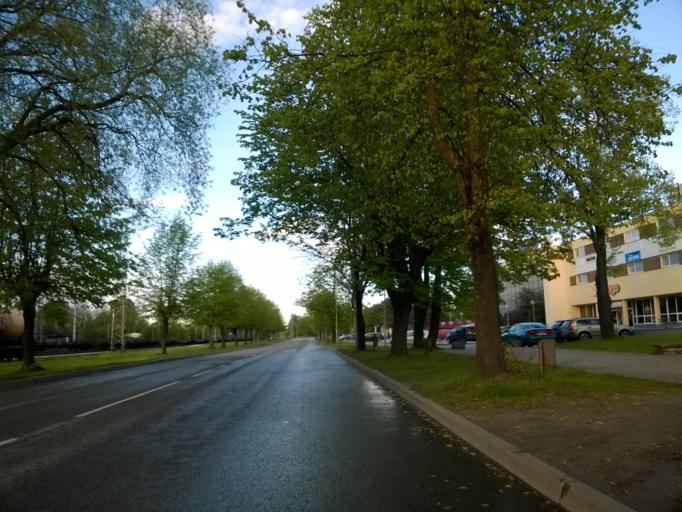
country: LV
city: Tireli
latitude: 56.9468
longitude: 23.6179
